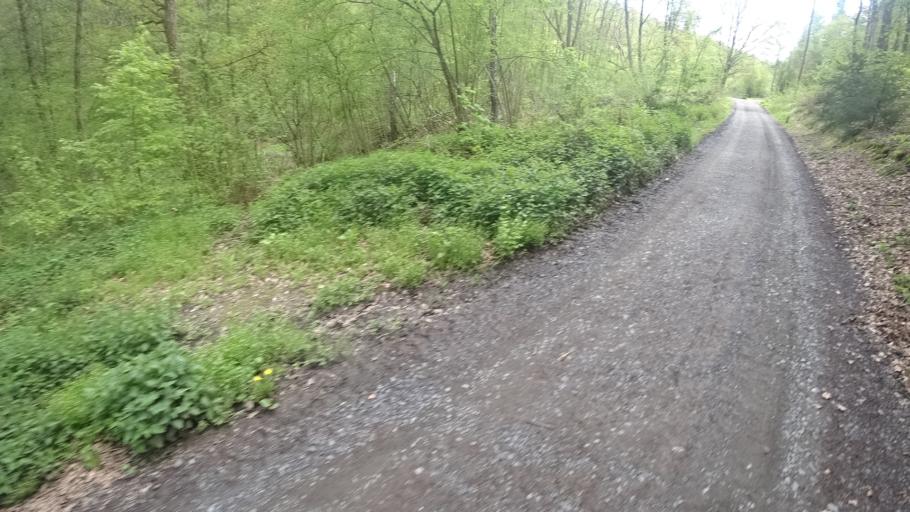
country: DE
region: Rheinland-Pfalz
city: Scheuerfeld
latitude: 50.7816
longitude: 7.8514
